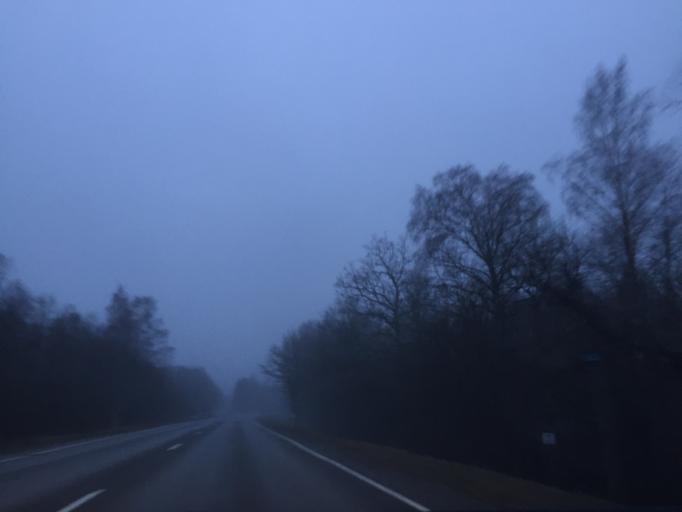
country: EE
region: Laeaene
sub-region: Lihula vald
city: Lihula
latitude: 58.6341
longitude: 23.6879
